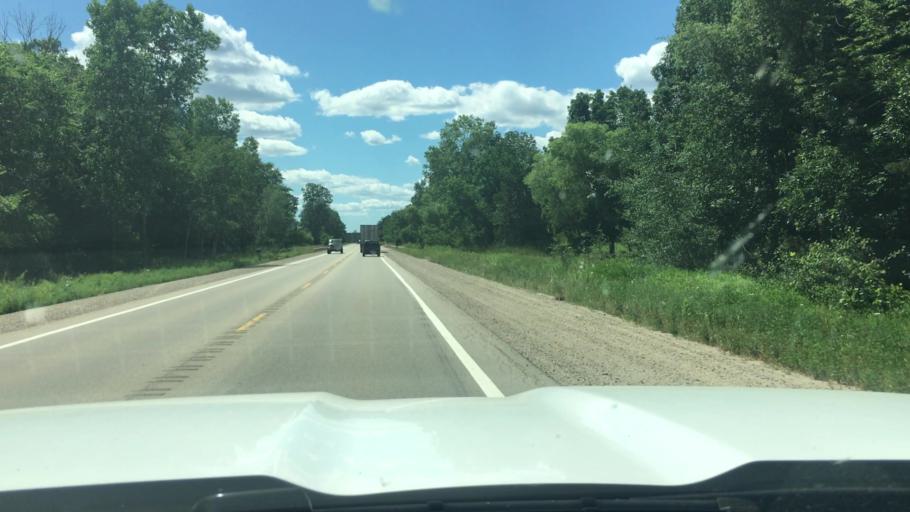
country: US
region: Michigan
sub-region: Kent County
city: Cedar Springs
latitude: 43.1760
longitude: -85.4714
